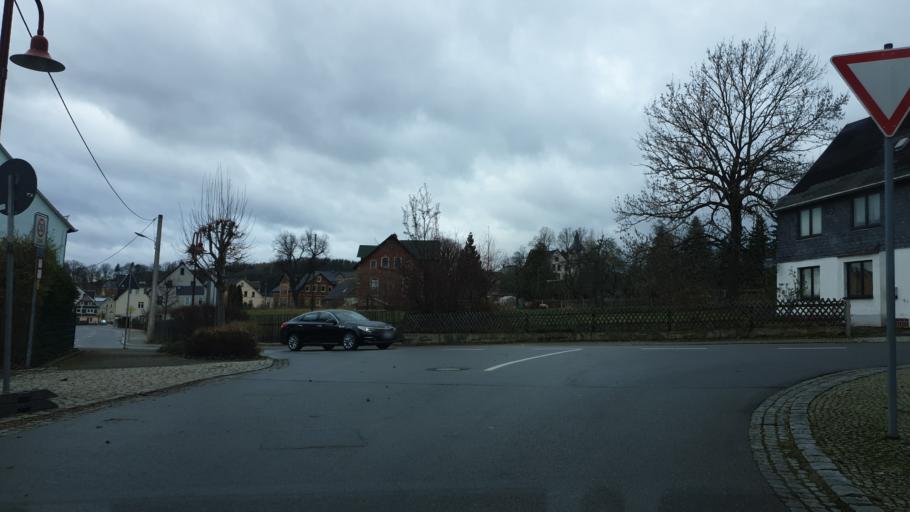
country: DE
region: Saxony
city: Hohndorf
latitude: 50.7459
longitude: 12.6690
